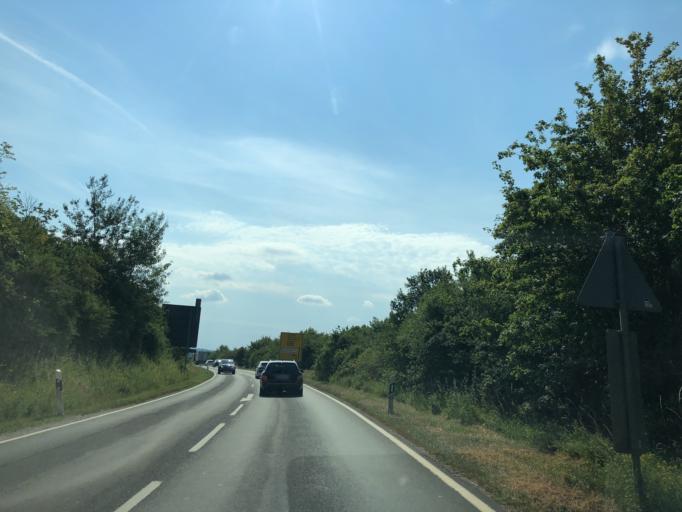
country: DE
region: Bavaria
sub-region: Upper Franconia
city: Schlusselfeld
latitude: 49.7462
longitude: 10.6368
